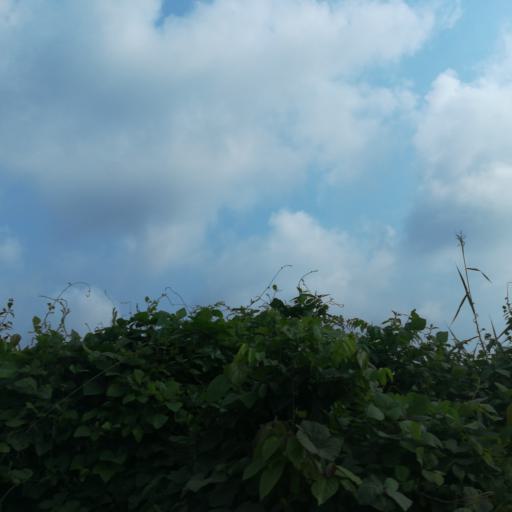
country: NG
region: Rivers
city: Okrika
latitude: 4.7827
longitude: 7.1434
